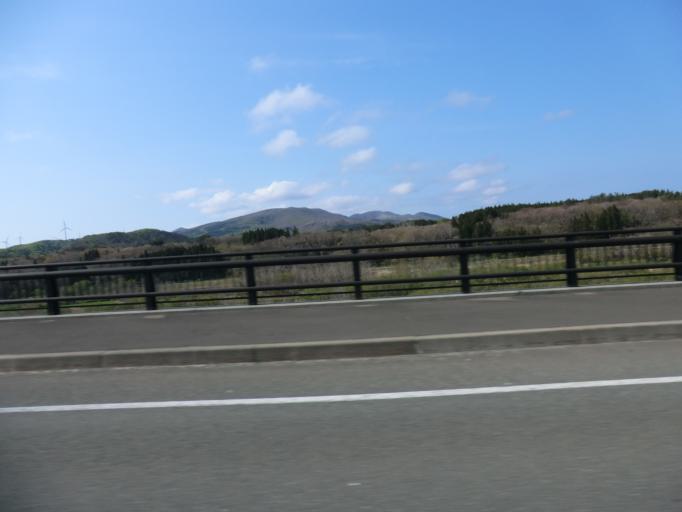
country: JP
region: Aomori
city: Misawa
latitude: 40.9810
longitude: 141.3597
